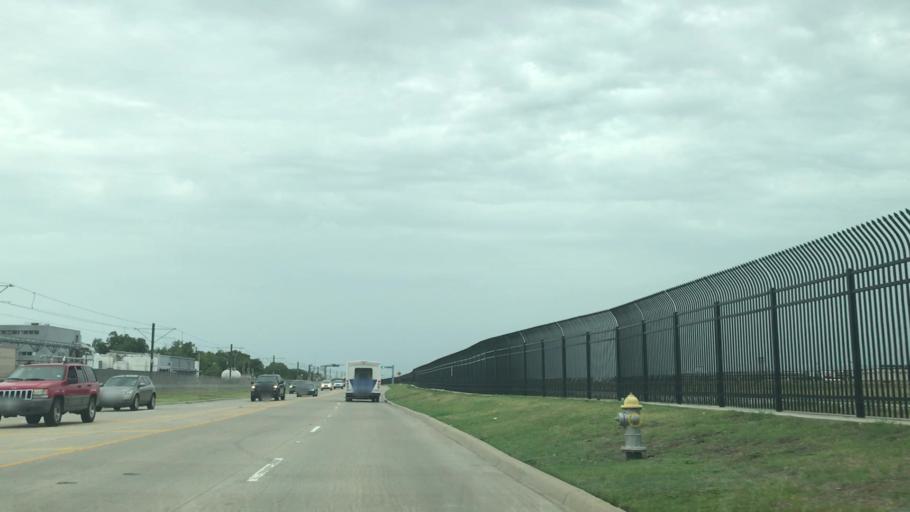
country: US
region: Texas
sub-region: Dallas County
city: University Park
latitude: 32.8320
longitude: -96.8434
